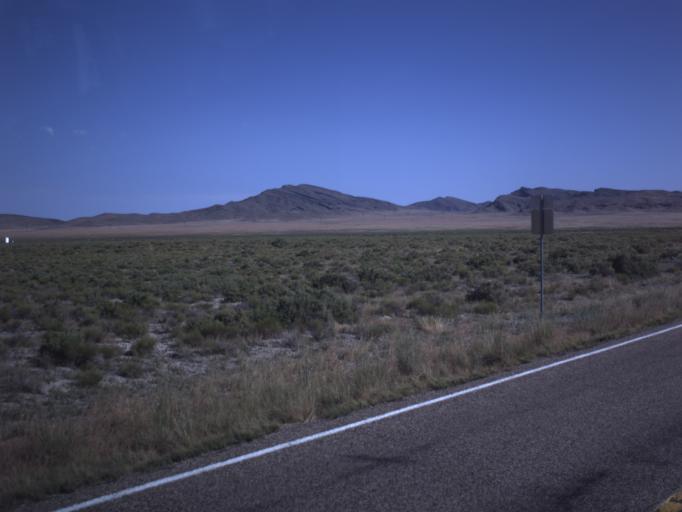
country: US
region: Utah
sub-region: Beaver County
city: Milford
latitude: 38.7106
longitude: -112.9698
